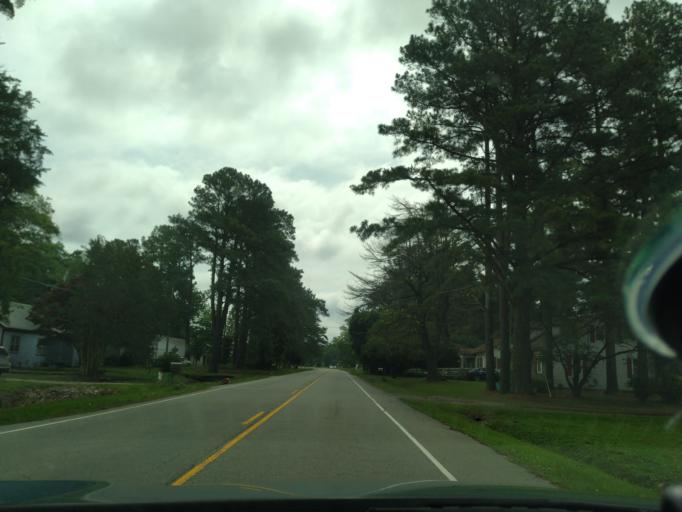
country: US
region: North Carolina
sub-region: Washington County
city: Plymouth
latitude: 35.8744
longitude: -76.6275
